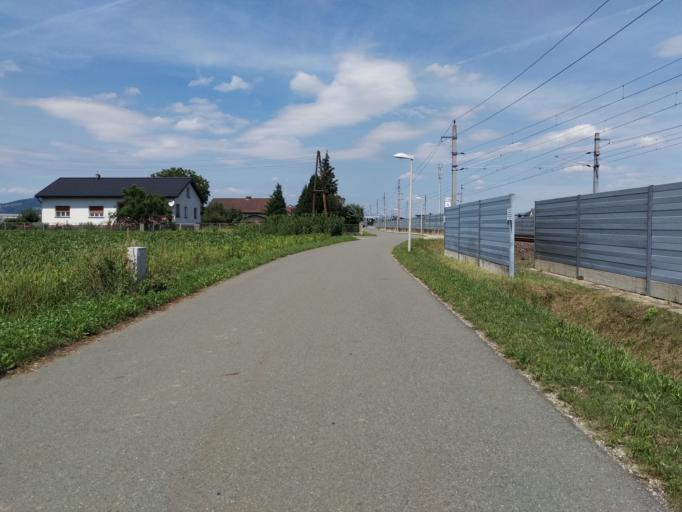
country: AT
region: Styria
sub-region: Politischer Bezirk Graz-Umgebung
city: Feldkirchen bei Graz
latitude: 46.9953
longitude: 15.4509
